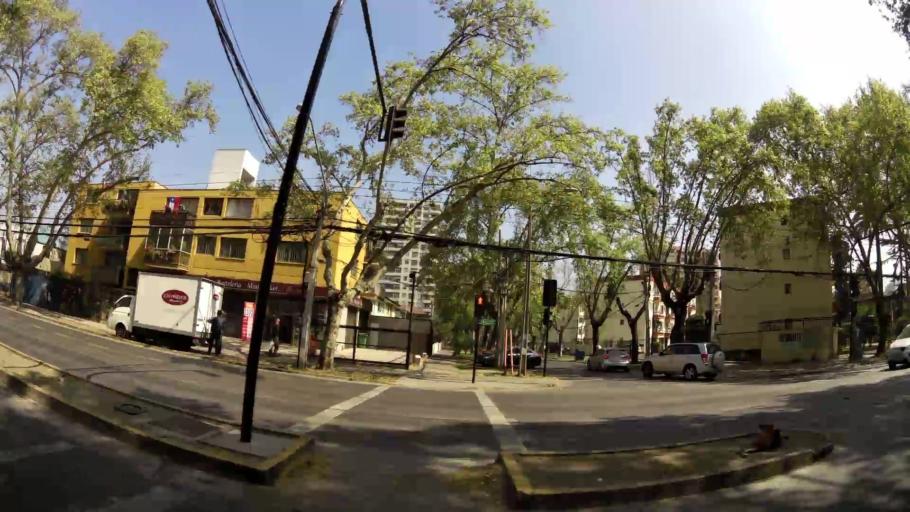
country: CL
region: Santiago Metropolitan
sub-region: Provincia de Santiago
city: Villa Presidente Frei, Nunoa, Santiago, Chile
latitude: -33.4619
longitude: -70.5981
